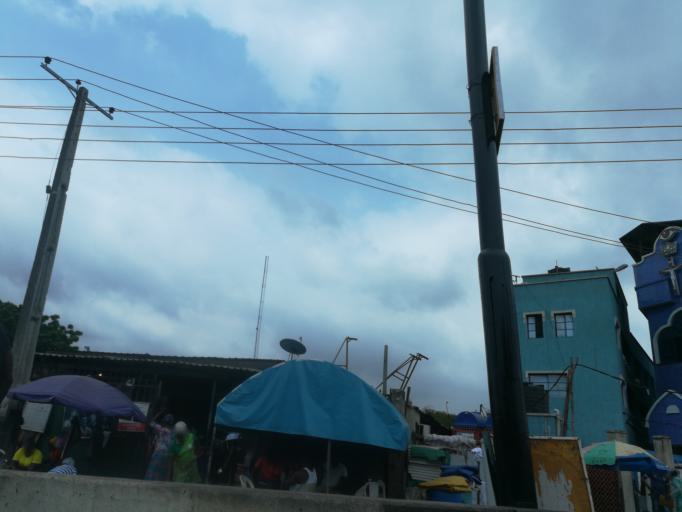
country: NG
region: Lagos
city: Lagos
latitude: 6.4557
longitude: 3.4056
